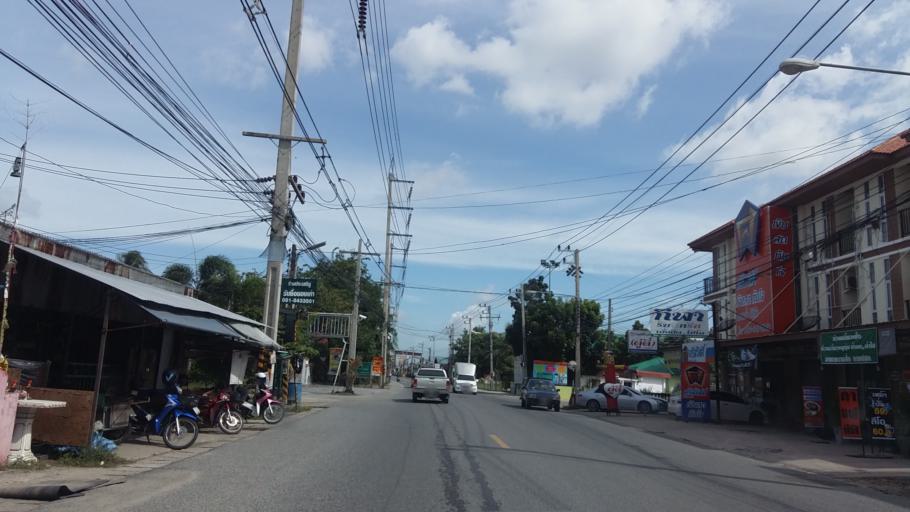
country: TH
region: Chon Buri
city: Phan Thong
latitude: 13.4332
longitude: 101.0620
